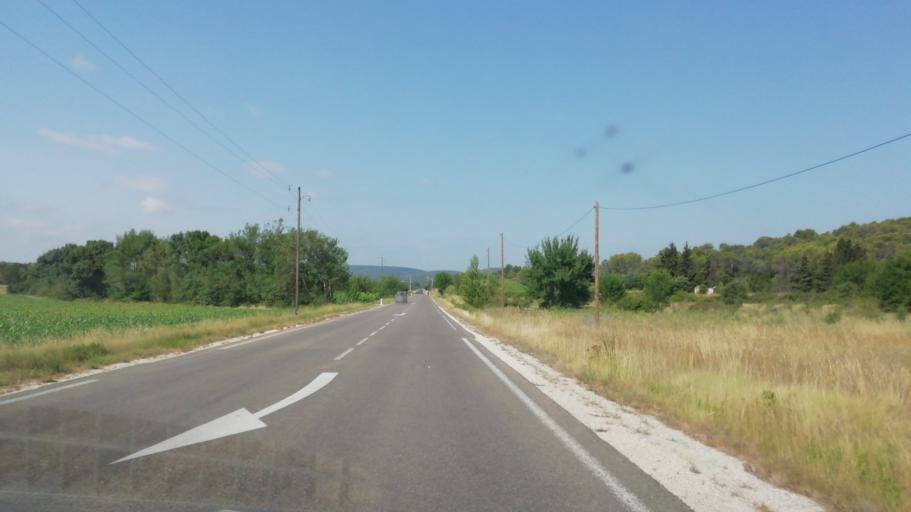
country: FR
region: Languedoc-Roussillon
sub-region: Departement de l'Herault
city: Les Matelles
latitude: 43.7389
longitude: 3.8355
